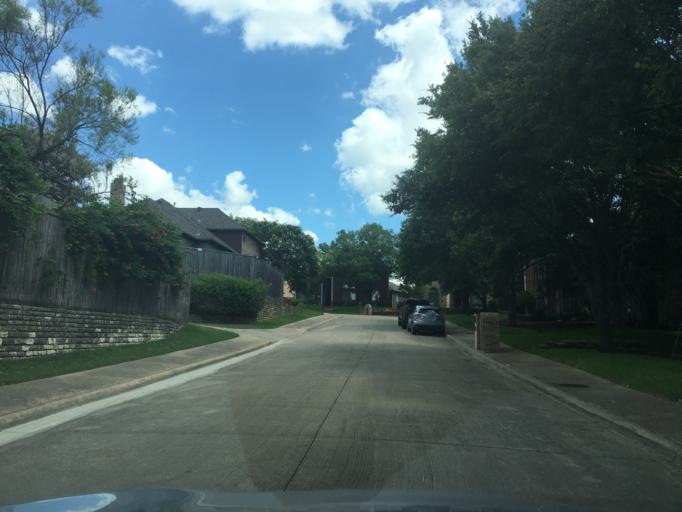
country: US
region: Texas
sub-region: Dallas County
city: Richardson
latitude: 32.8703
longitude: -96.7139
